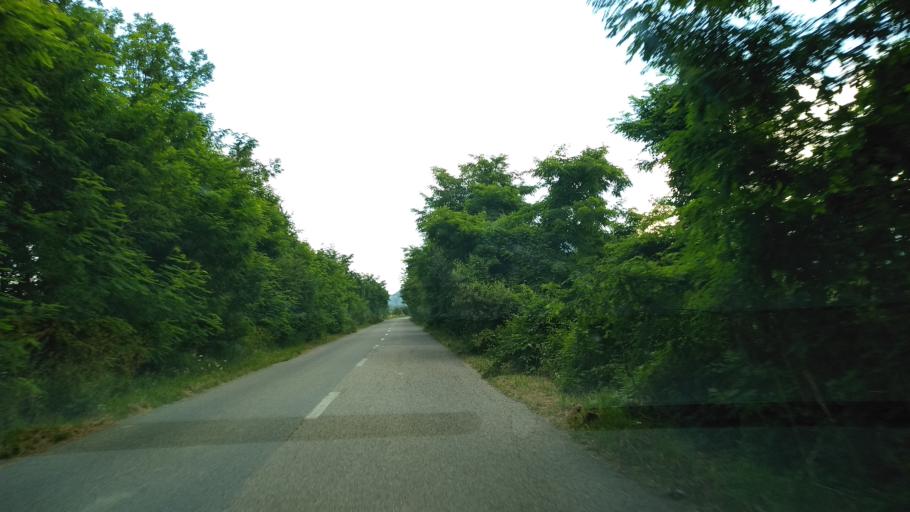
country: RO
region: Hunedoara
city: Salasu de Sus
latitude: 45.5145
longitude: 22.9573
